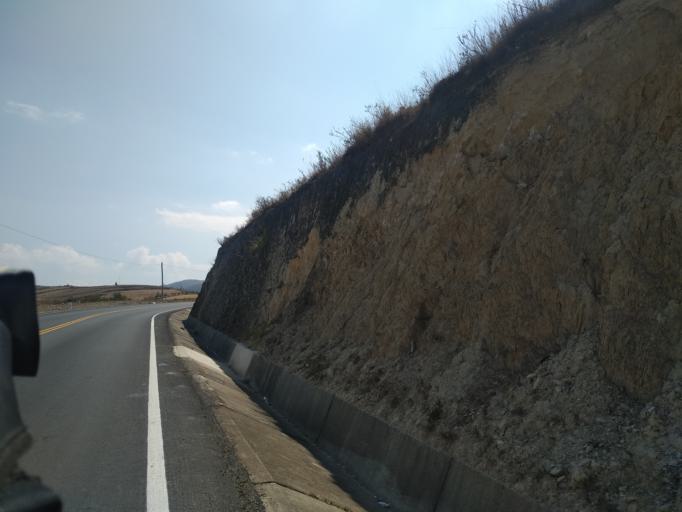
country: PE
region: Cajamarca
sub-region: Provincia de Cajamarca
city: Llacanora
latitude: -7.2070
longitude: -78.3932
